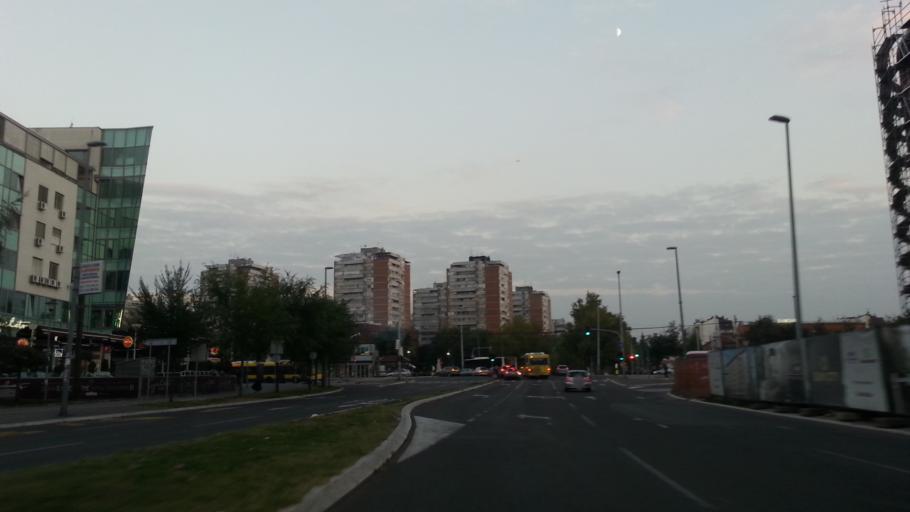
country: RS
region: Central Serbia
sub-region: Belgrade
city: Novi Beograd
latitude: 44.8043
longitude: 20.3875
